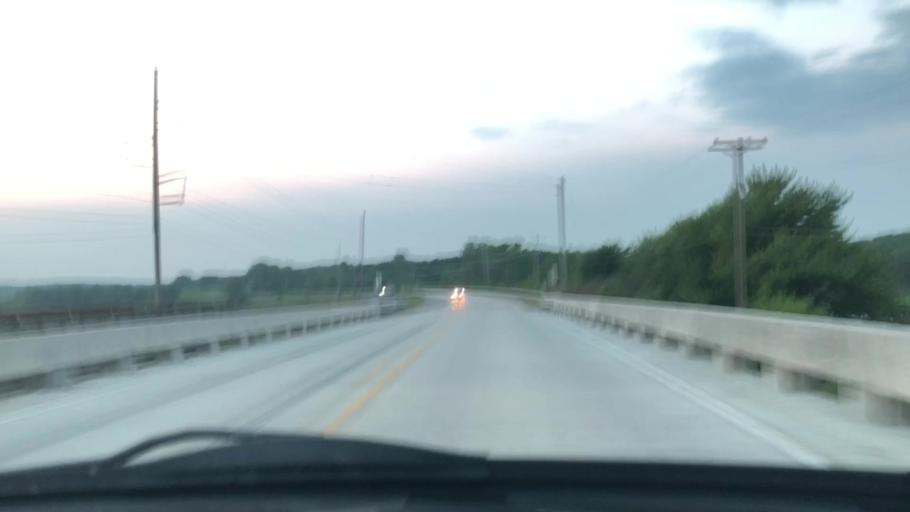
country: US
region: Iowa
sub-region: Johnson County
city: North Liberty
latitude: 41.8069
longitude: -91.6520
